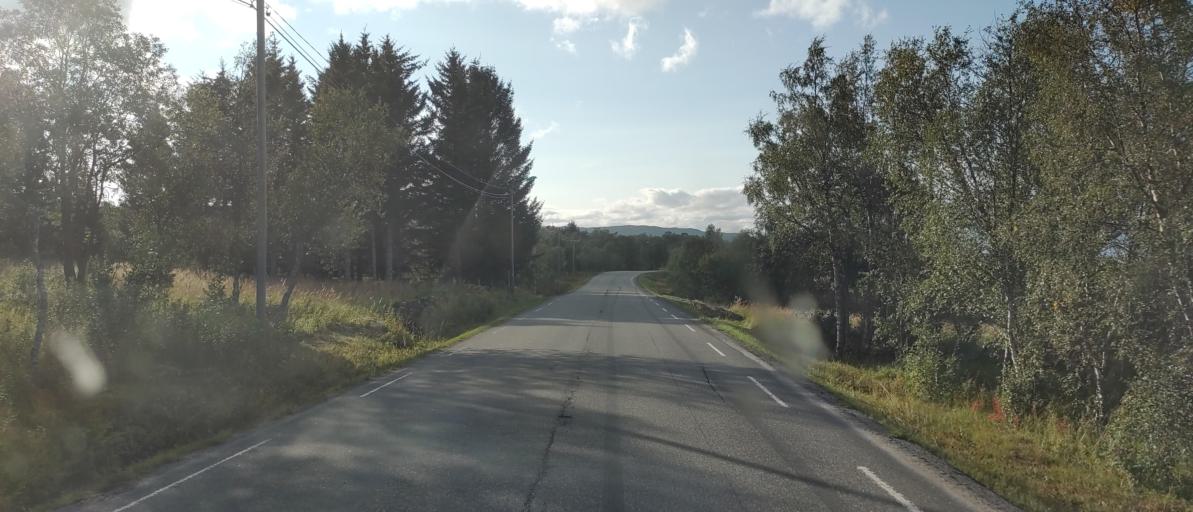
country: NO
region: Nordland
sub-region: Sortland
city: Sortland
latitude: 68.7211
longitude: 15.5045
